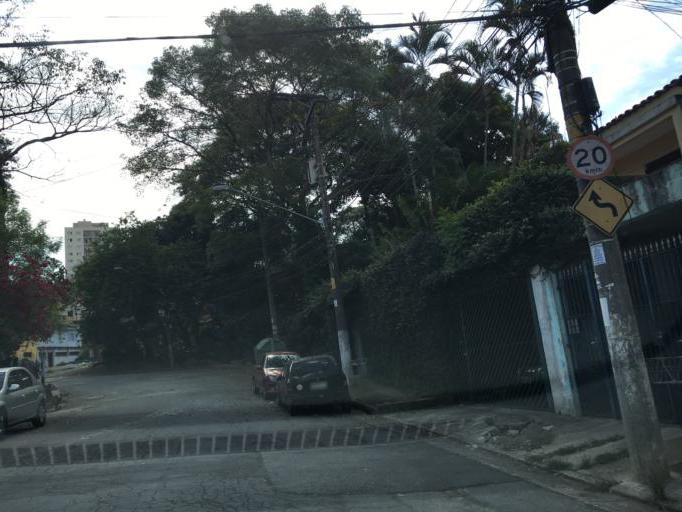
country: BR
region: Sao Paulo
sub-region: Osasco
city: Osasco
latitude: -23.5764
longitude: -46.7349
